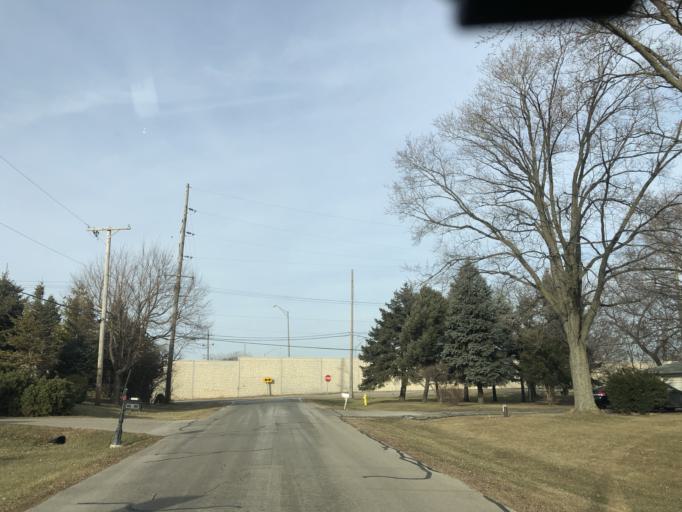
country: US
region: Illinois
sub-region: Cook County
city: Lemont
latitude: 41.7140
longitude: -88.0100
